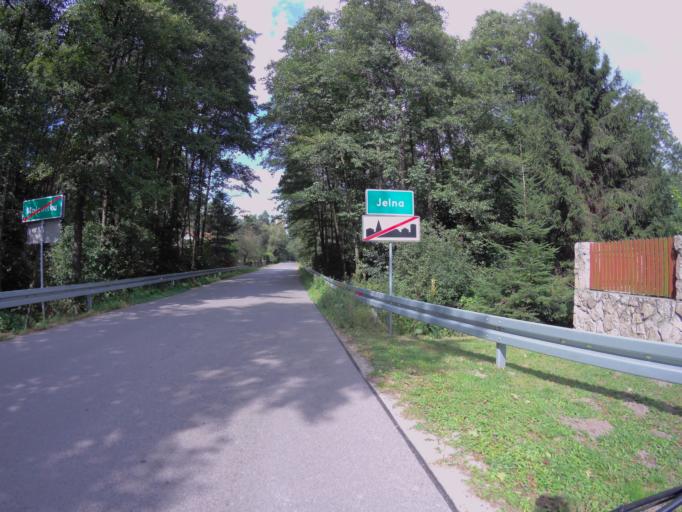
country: PL
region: Subcarpathian Voivodeship
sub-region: Powiat lezajski
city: Brzoza Krolewska
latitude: 50.2744
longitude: 22.3527
